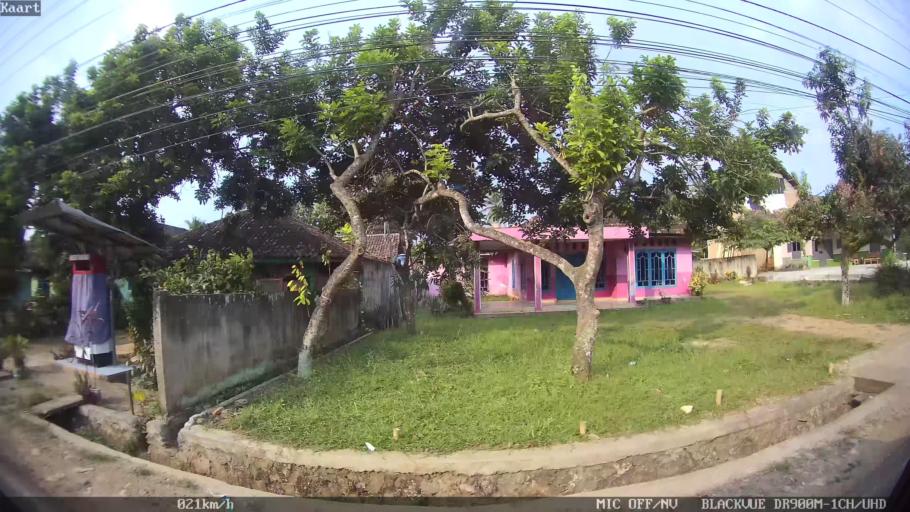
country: ID
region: Lampung
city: Natar
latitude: -5.3679
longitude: 105.1901
